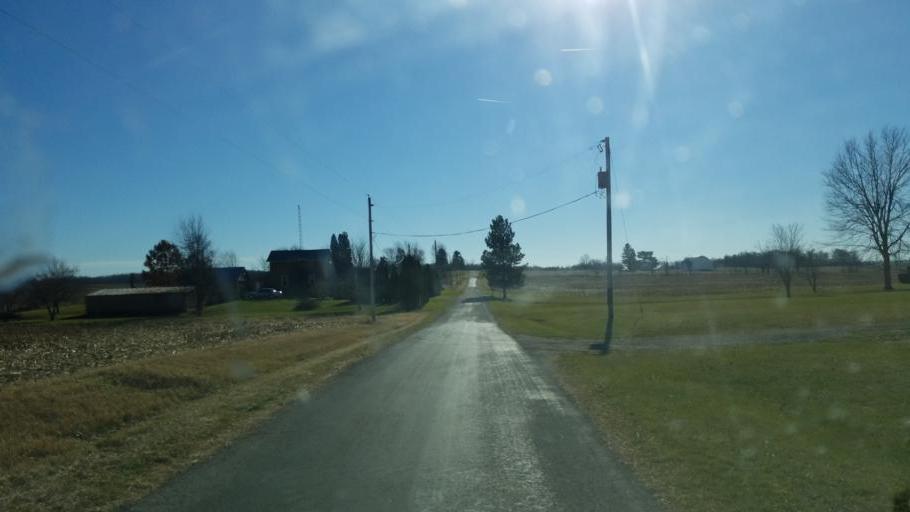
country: US
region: Ohio
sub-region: Crawford County
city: Crestline
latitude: 40.8830
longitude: -82.8082
